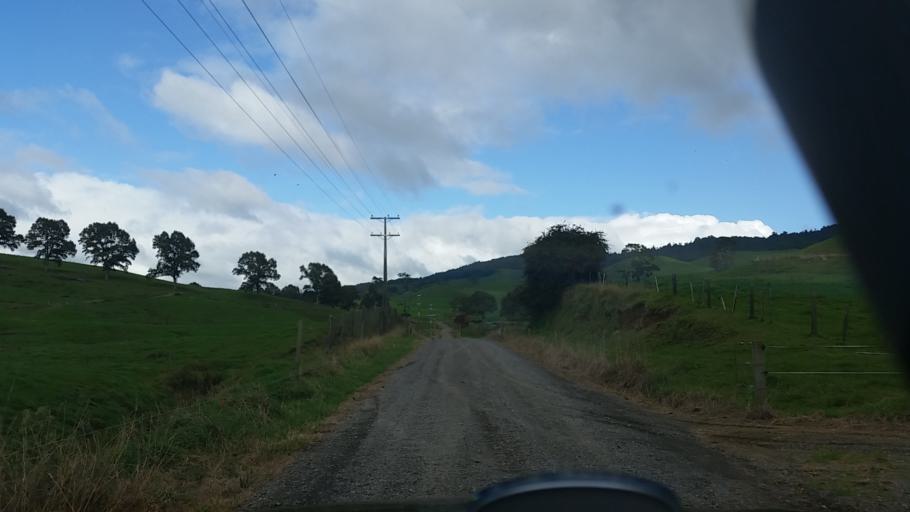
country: NZ
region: Waikato
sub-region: Matamata-Piako District
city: Matamata
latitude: -37.8111
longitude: 175.6730
